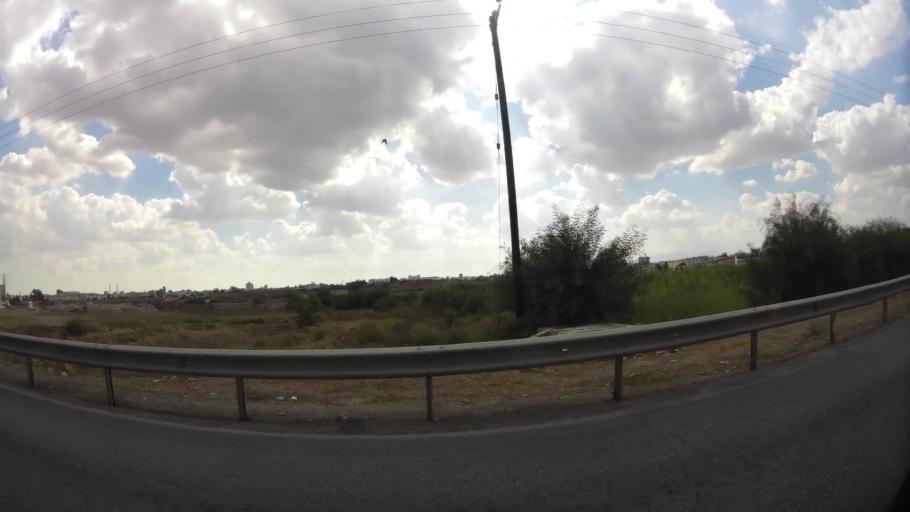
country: CY
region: Lefkosia
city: Nicosia
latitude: 35.2089
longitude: 33.3543
